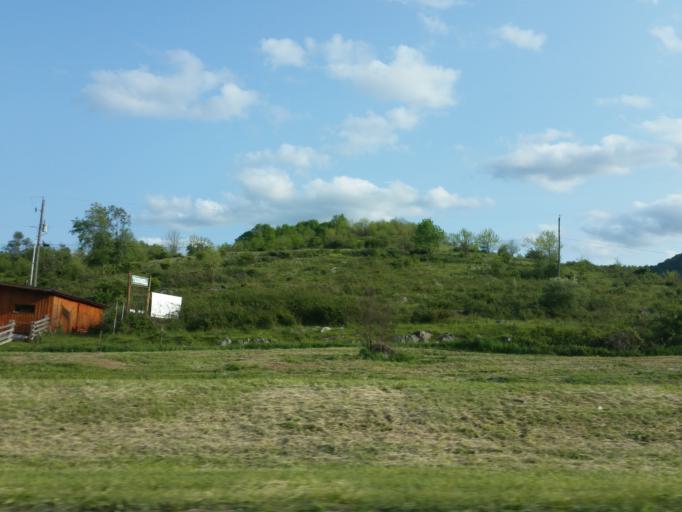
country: US
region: Virginia
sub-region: Tazewell County
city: Tazewell
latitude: 37.1196
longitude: -81.5825
